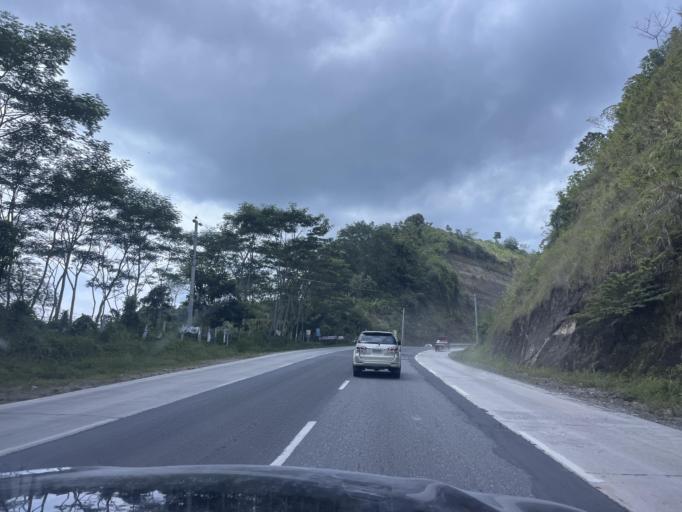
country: PH
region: Davao
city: Simod
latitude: 7.3747
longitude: 125.2781
